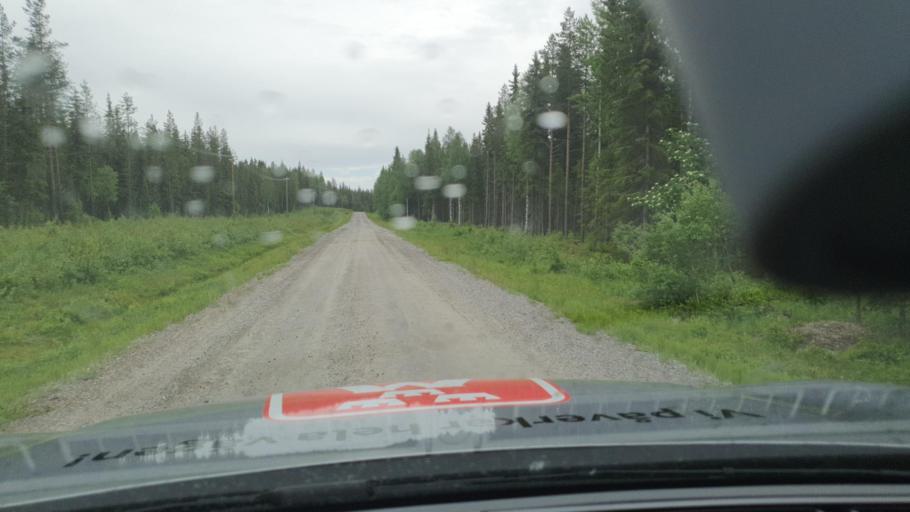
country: SE
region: Norrbotten
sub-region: Kalix Kommun
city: Rolfs
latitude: 66.0386
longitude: 23.0567
